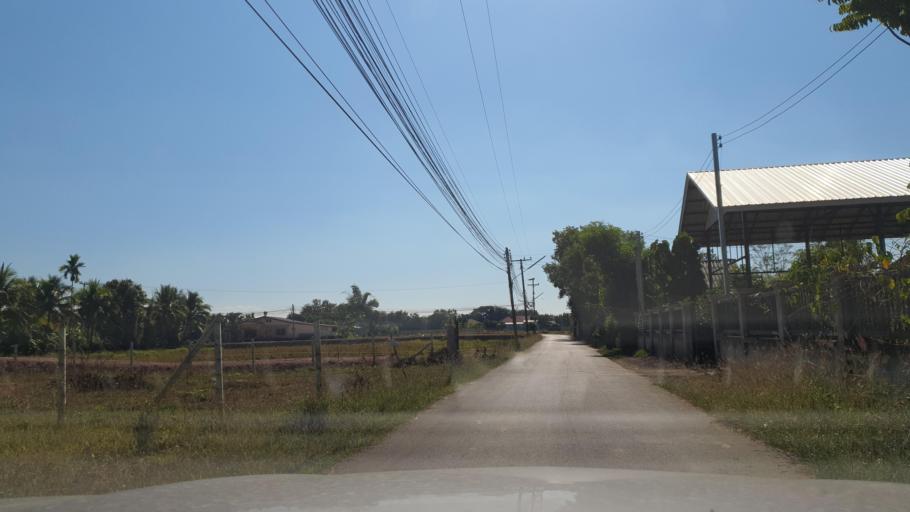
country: TH
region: Chiang Mai
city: San Pa Tong
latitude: 18.6425
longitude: 98.8784
